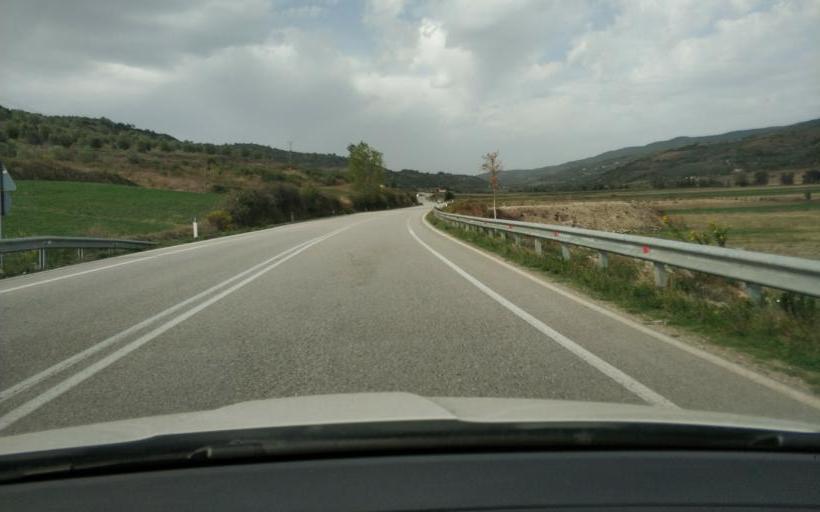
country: AL
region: Gjirokaster
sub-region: Rrethi i Tepelenes
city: Krahes
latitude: 40.4417
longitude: 19.8485
